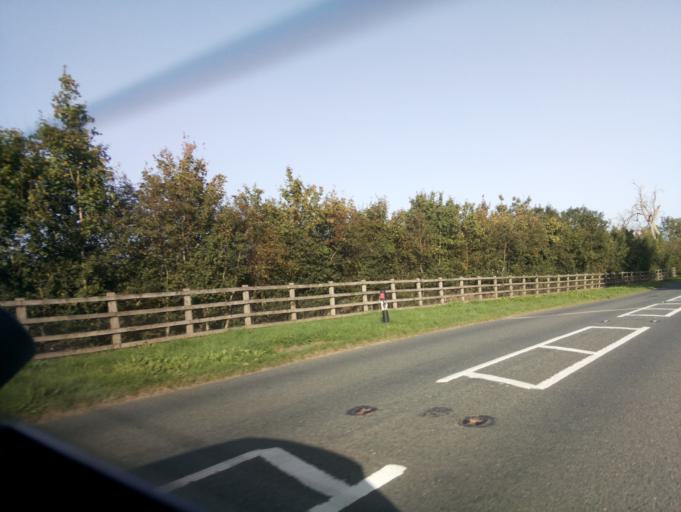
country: GB
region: England
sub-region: Gloucestershire
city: Gloucester
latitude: 51.9616
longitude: -2.2637
